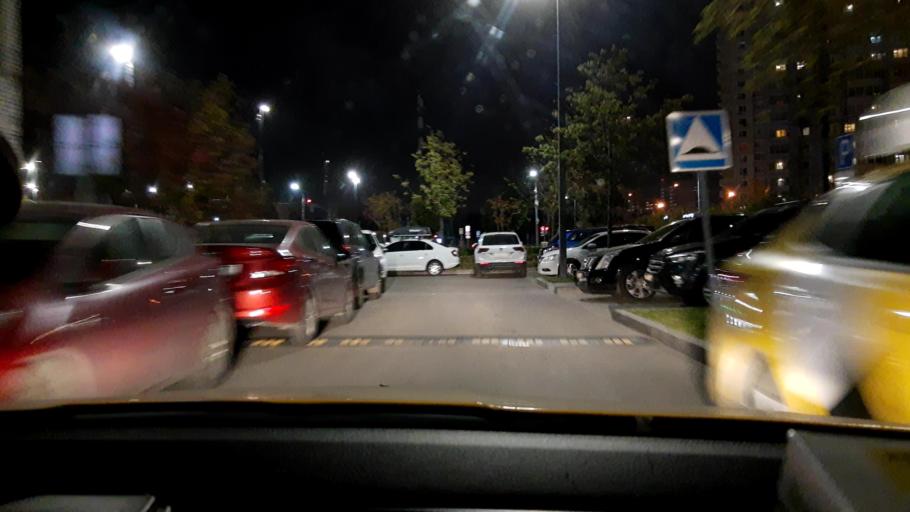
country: RU
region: Moskovskaya
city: Kommunarka
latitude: 55.5426
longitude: 37.4880
